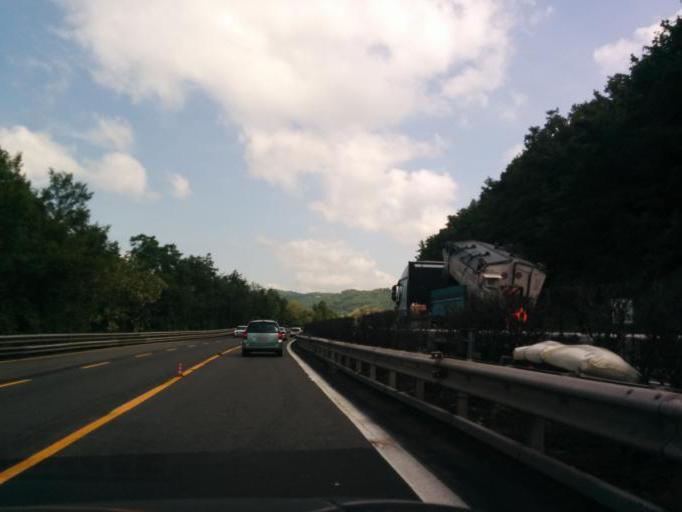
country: IT
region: Emilia-Romagna
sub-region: Provincia di Bologna
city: San Benedetto Val di Sambro
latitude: 44.1672
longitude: 11.2094
